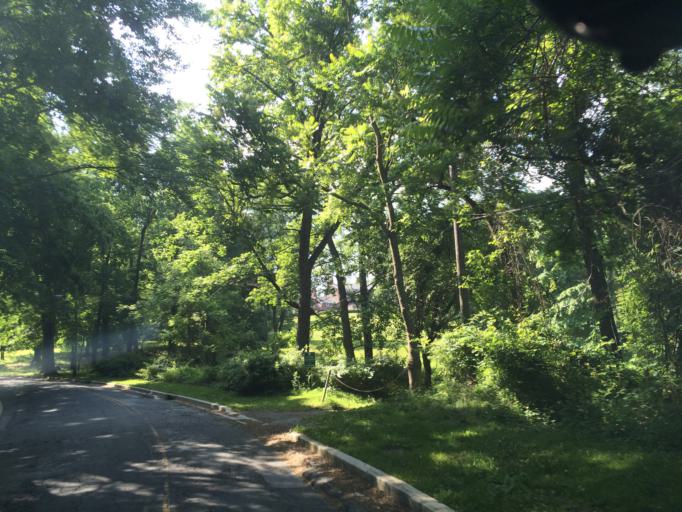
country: US
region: Maryland
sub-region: Baltimore County
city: Towson
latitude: 39.3521
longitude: -76.6399
